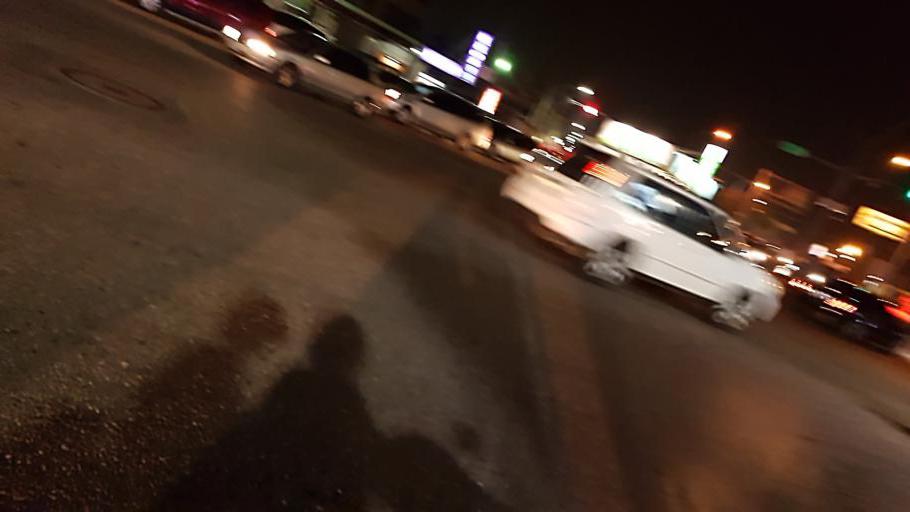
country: TW
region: Taiwan
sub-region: Changhua
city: Chang-hua
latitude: 24.0683
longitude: 120.5258
